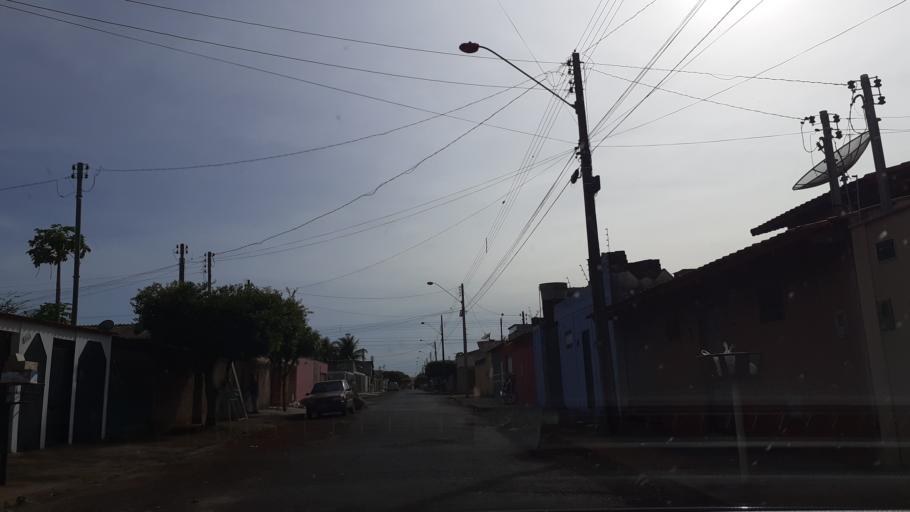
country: BR
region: Goias
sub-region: Itumbiara
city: Itumbiara
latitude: -18.4219
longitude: -49.2473
